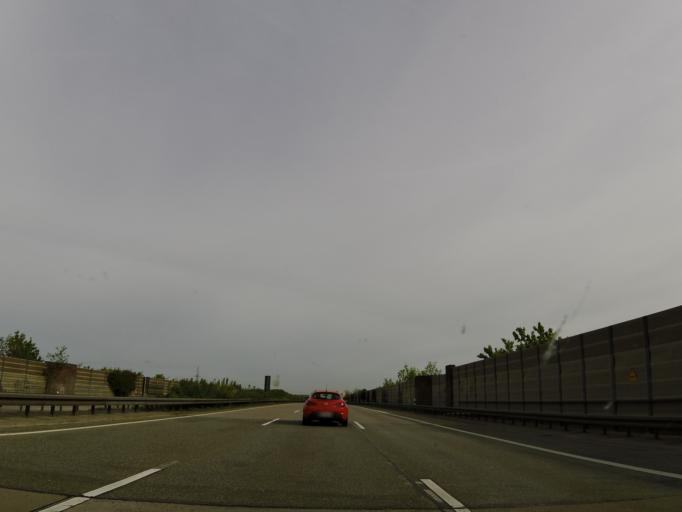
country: DE
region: Lower Saxony
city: Hildesheim
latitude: 52.1651
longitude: 9.9857
